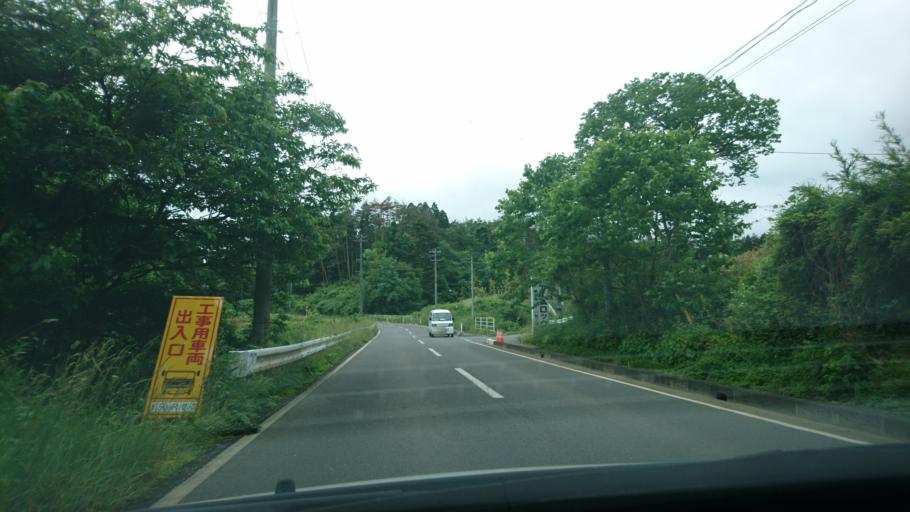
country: JP
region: Iwate
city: Ichinoseki
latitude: 38.9575
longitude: 141.0547
